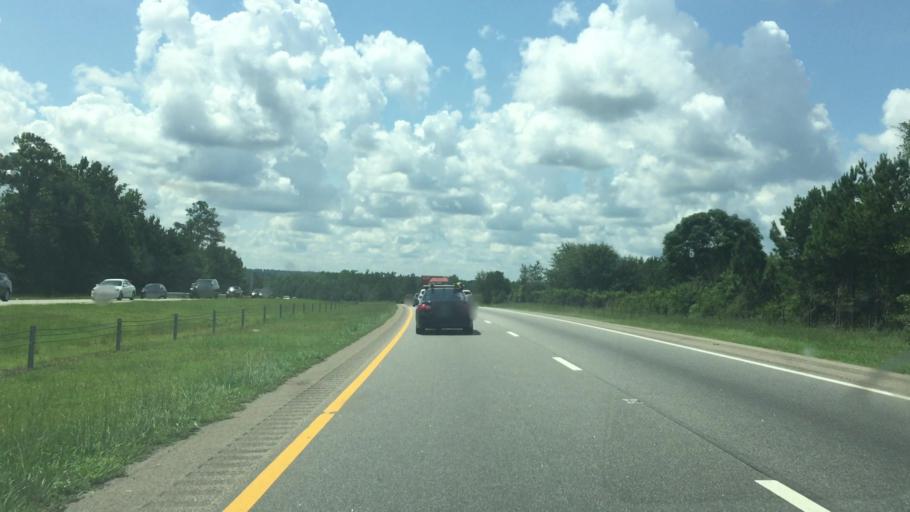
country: US
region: North Carolina
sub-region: Richmond County
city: Cordova
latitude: 34.8961
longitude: -79.7911
